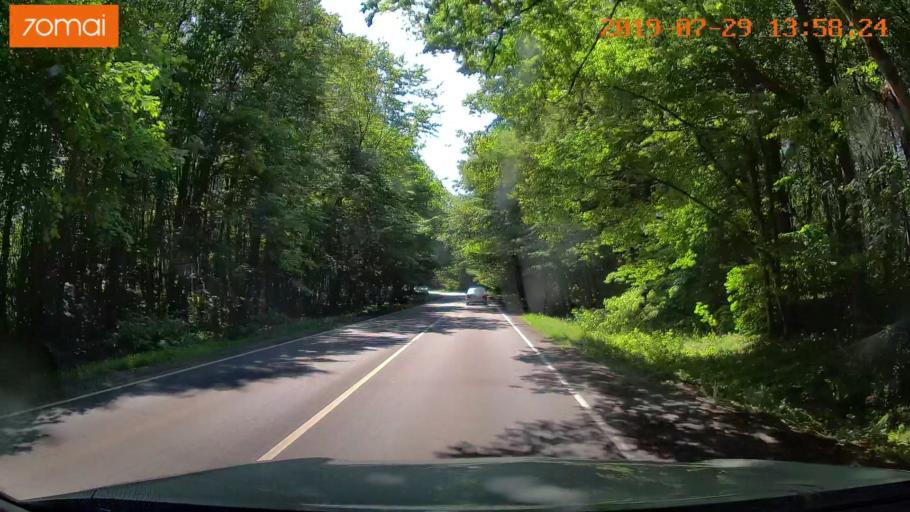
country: RU
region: Kaliningrad
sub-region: Gorod Kaliningrad
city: Baltiysk
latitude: 54.6939
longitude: 19.9371
